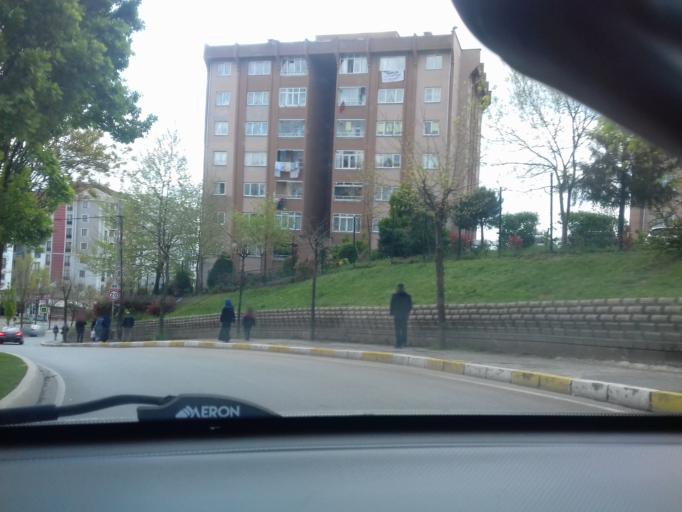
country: TR
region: Istanbul
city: Pendik
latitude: 40.9065
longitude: 29.2785
